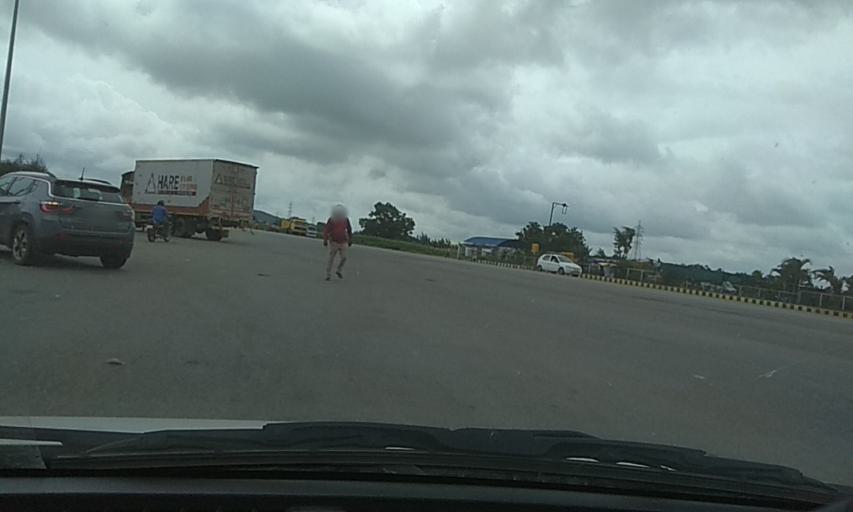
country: IN
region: Karnataka
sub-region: Davanagere
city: Mayakonda
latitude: 14.3758
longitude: 76.1070
